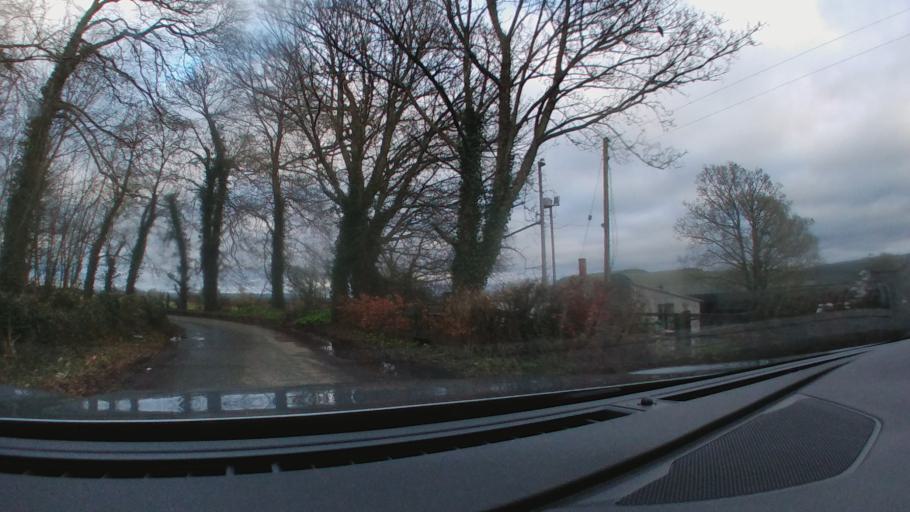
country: IE
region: Leinster
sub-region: Kilkenny
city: Thomastown
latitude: 52.5610
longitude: -7.1364
